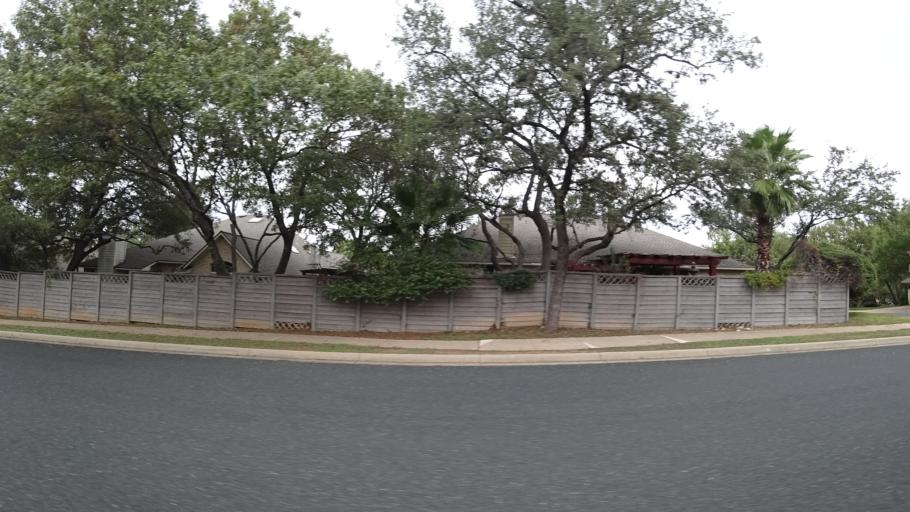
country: US
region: Texas
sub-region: Williamson County
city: Brushy Creek
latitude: 30.5135
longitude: -97.7447
